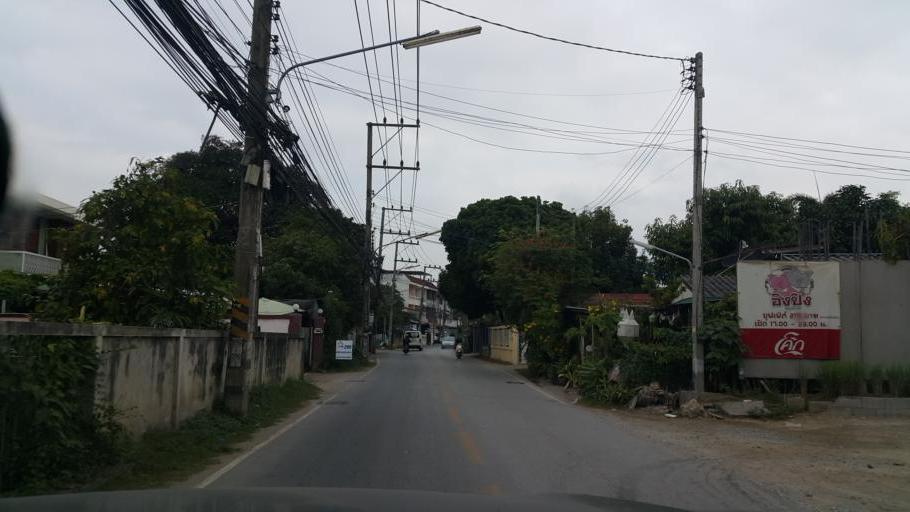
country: TH
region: Chiang Mai
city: Chiang Mai
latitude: 18.8065
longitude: 99.0028
